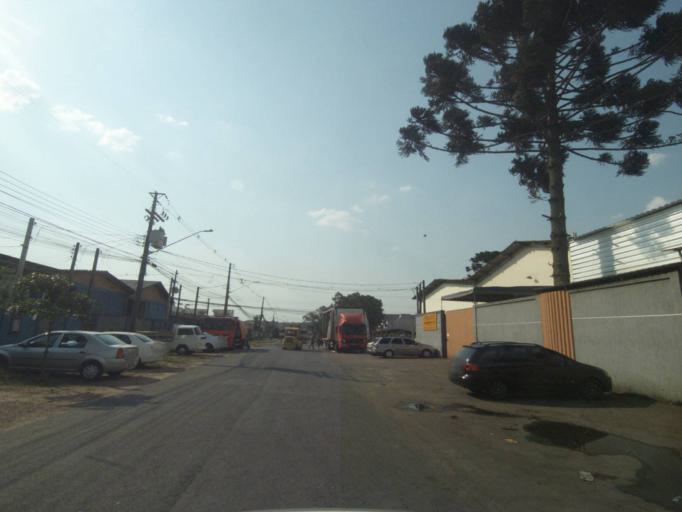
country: BR
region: Parana
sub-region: Sao Jose Dos Pinhais
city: Sao Jose dos Pinhais
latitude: -25.5348
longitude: -49.2352
